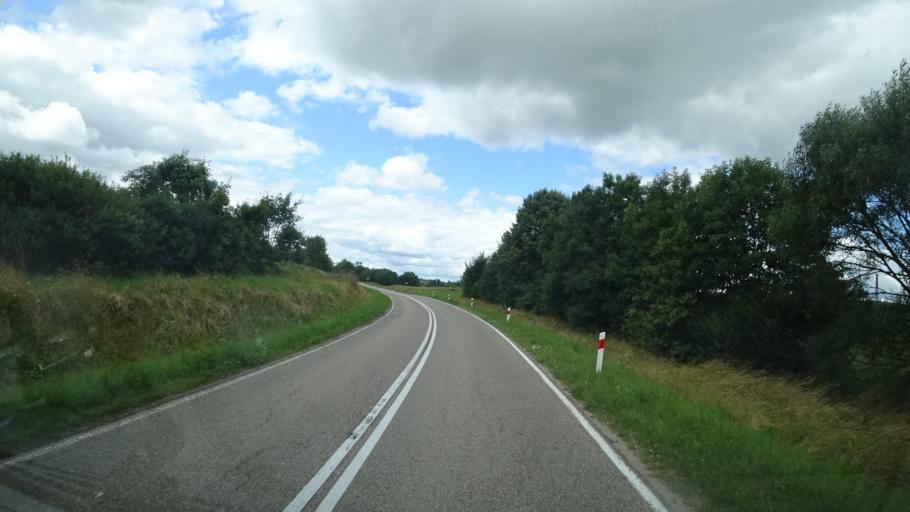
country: PL
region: Warmian-Masurian Voivodeship
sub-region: Powiat goldapski
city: Banie Mazurskie
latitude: 54.2092
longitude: 22.1838
